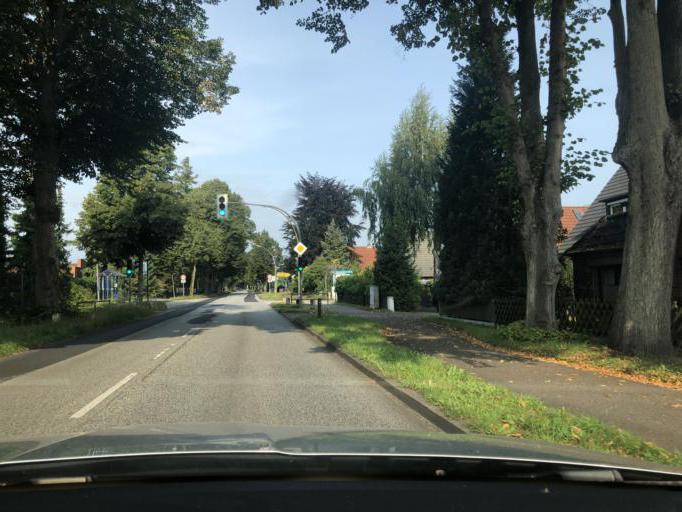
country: DE
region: Schleswig-Holstein
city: Gross Gronau
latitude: 53.8107
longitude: 10.7454
